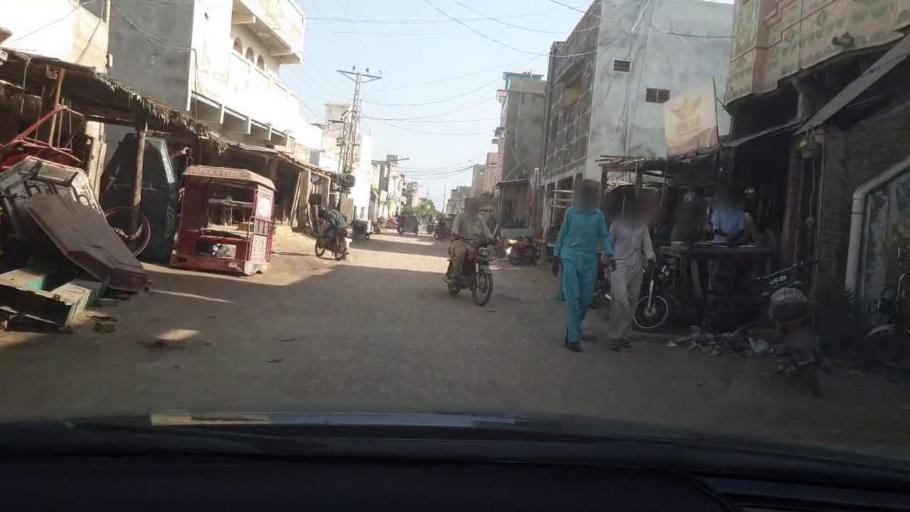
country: PK
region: Sindh
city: Naukot
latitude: 24.7640
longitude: 69.1985
